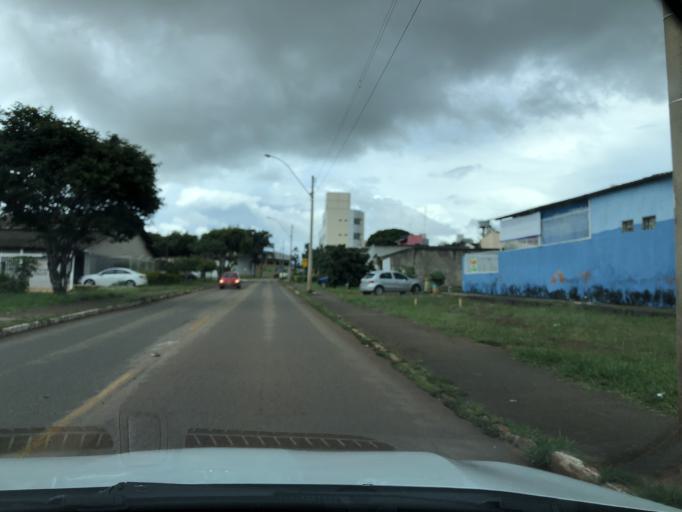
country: BR
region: Goias
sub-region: Luziania
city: Luziania
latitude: -16.0265
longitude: -48.0639
